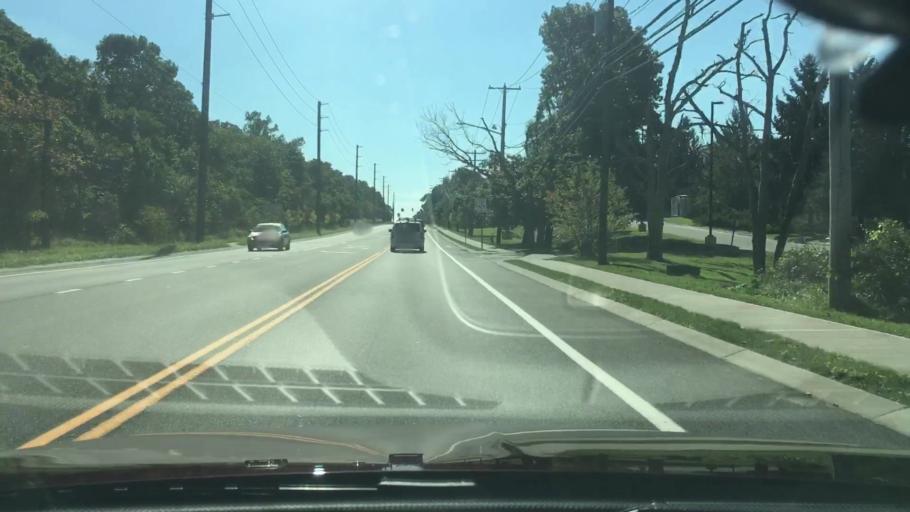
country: US
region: New York
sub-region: Suffolk County
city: Coram
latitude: 40.8600
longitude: -72.9987
